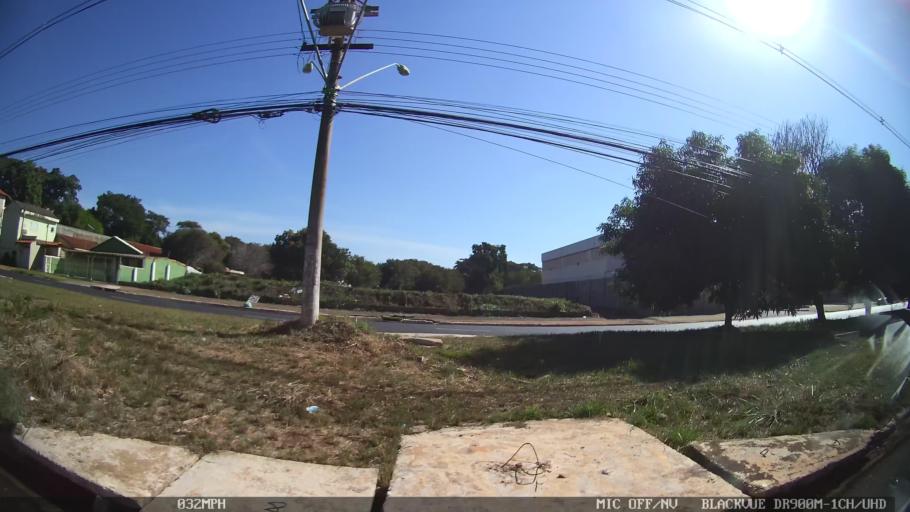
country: BR
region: Sao Paulo
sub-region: Ribeirao Preto
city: Ribeirao Preto
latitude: -21.1860
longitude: -47.7609
